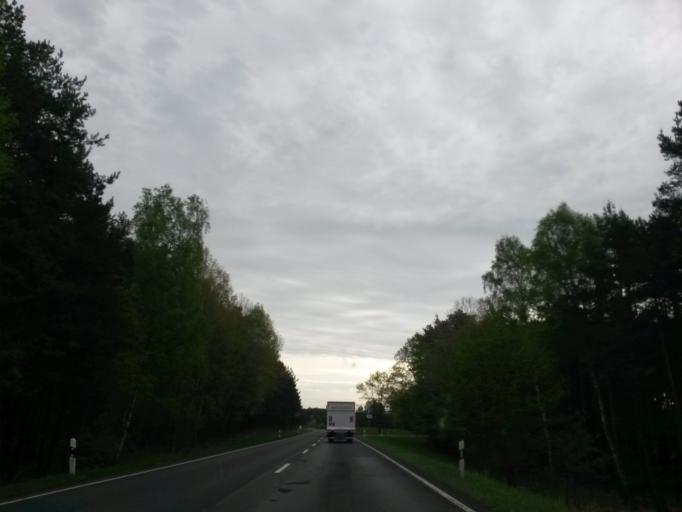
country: DE
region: Bavaria
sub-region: Upper Franconia
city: Frensdorf
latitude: 49.7771
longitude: 10.9027
